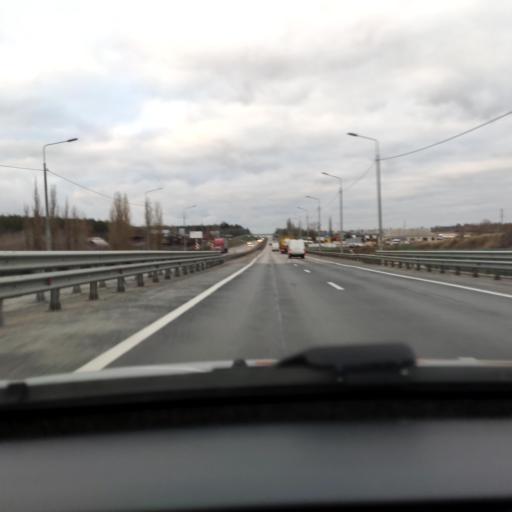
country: RU
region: Voronezj
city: Ramon'
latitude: 51.9399
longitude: 39.2216
